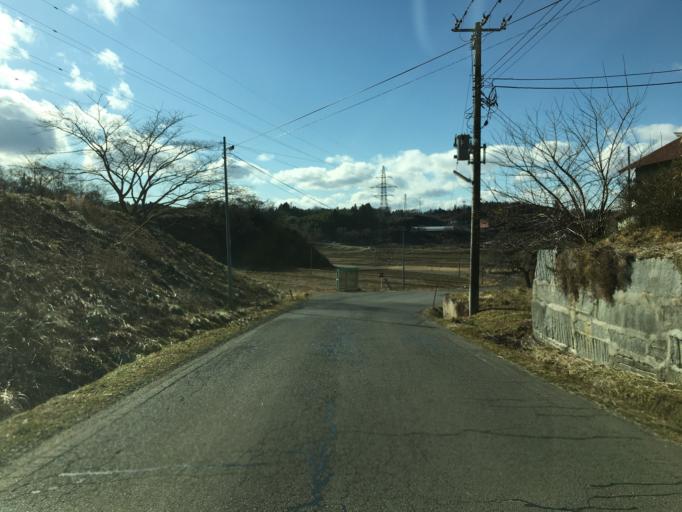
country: JP
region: Fukushima
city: Funehikimachi-funehiki
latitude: 37.4340
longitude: 140.5566
